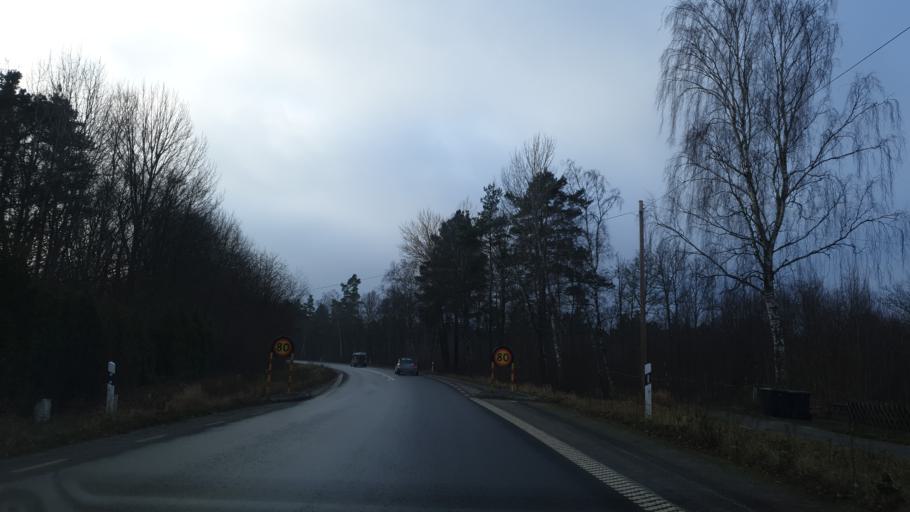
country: SE
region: Blekinge
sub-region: Karlshamns Kommun
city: Morrum
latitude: 56.1492
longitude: 14.6692
